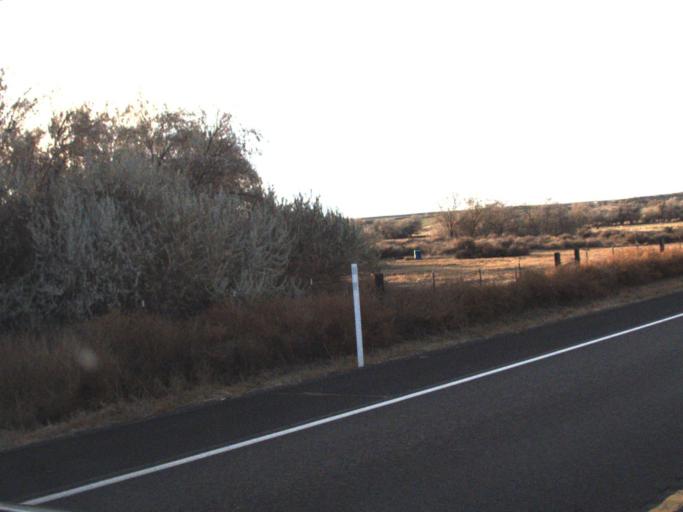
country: US
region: Washington
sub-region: Walla Walla County
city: Garrett
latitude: 46.0450
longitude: -118.6942
